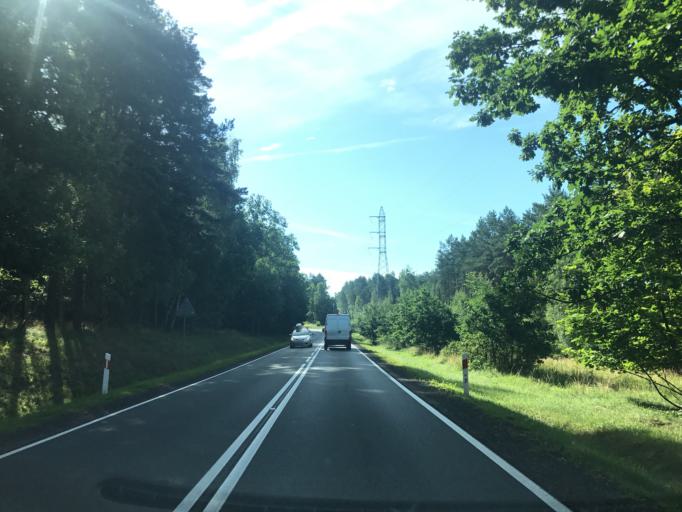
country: PL
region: Pomeranian Voivodeship
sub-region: Powiat czluchowski
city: Przechlewo
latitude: 53.7314
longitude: 17.2183
